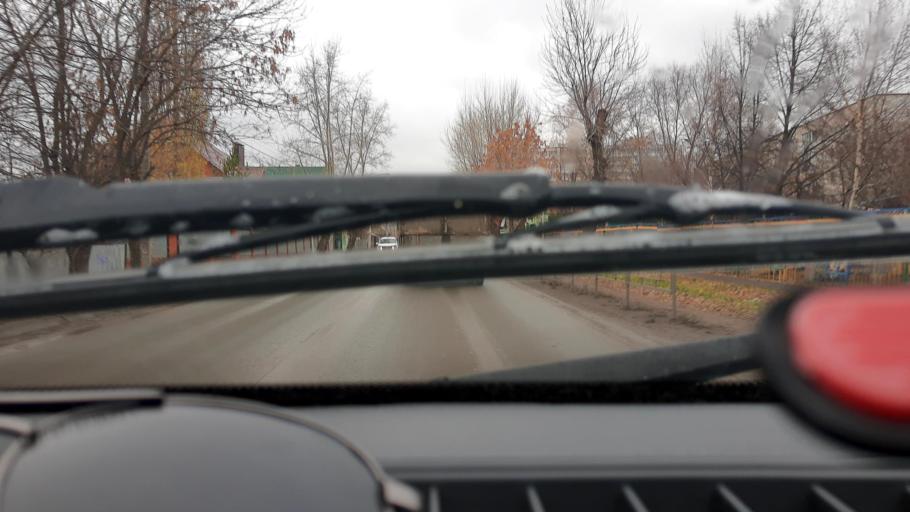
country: RU
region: Bashkortostan
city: Avdon
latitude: 54.6985
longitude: 55.8243
